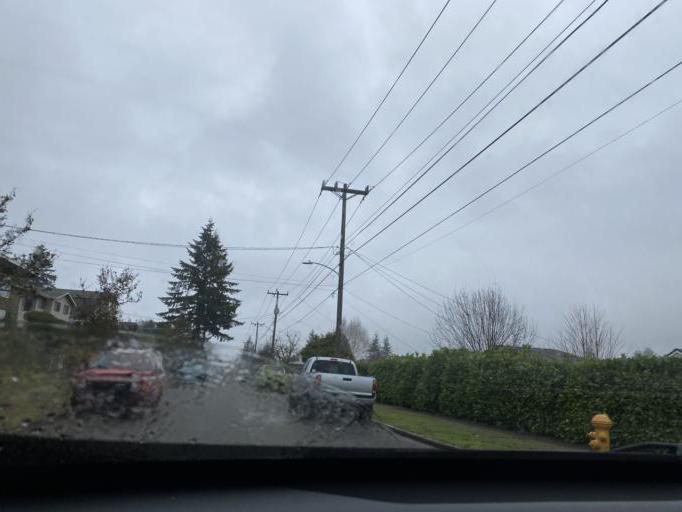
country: US
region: Washington
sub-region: King County
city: Seattle
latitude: 47.6505
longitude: -122.4023
